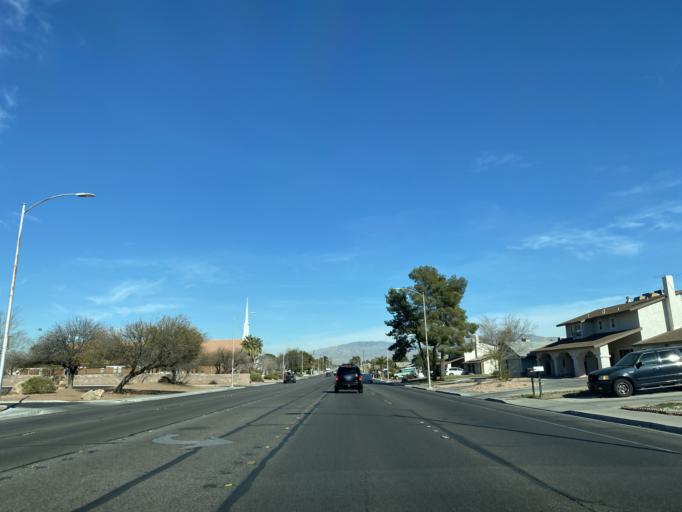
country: US
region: Nevada
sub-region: Clark County
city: Las Vegas
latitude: 36.2046
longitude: -115.2239
